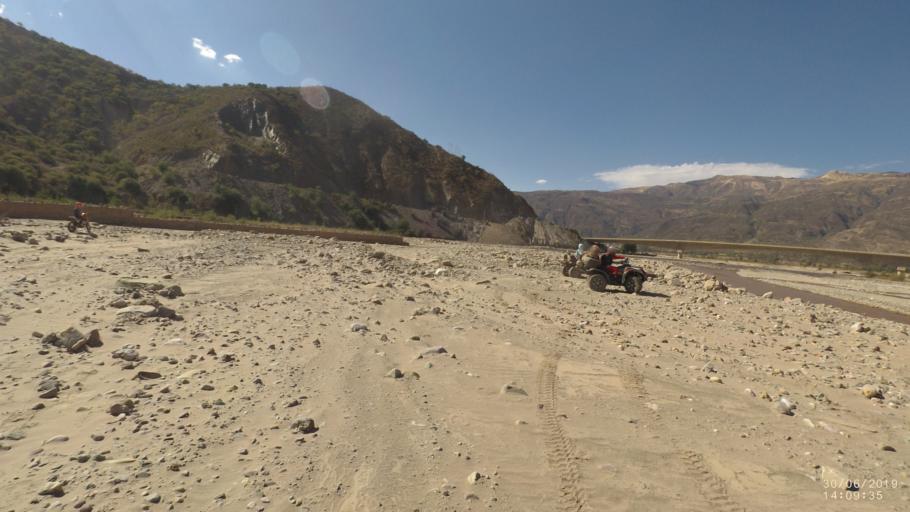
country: BO
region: Cochabamba
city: Irpa Irpa
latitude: -17.8006
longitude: -66.3533
